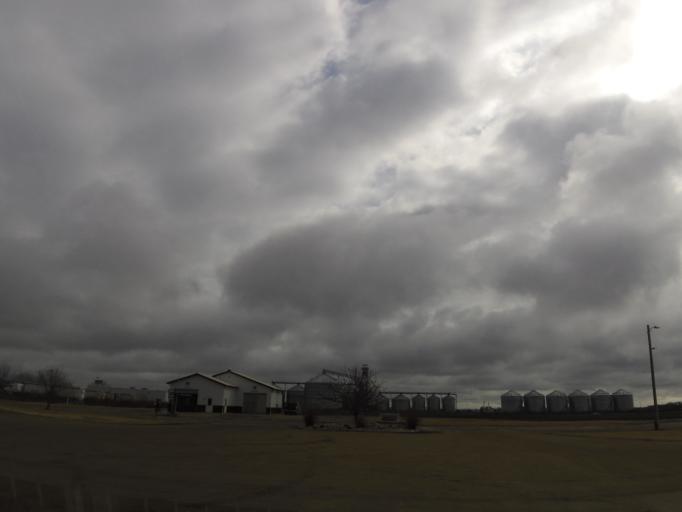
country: US
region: North Dakota
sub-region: Traill County
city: Mayville
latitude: 47.4963
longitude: -97.3136
